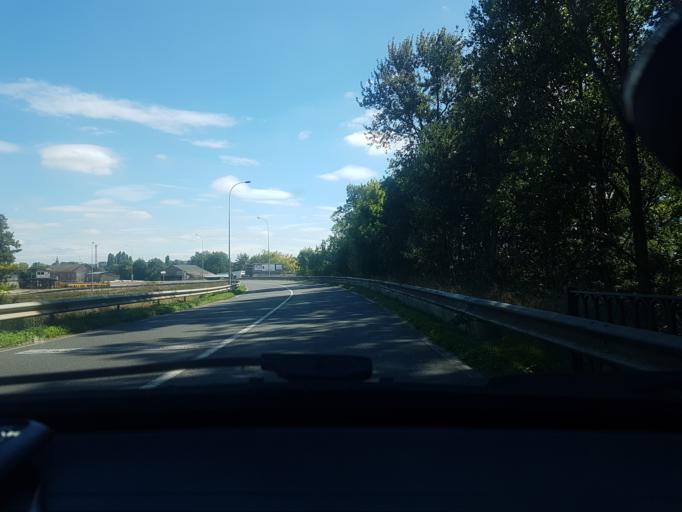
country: FR
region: Franche-Comte
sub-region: Departement de la Haute-Saone
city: Gray-la-Ville
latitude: 47.4488
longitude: 5.5644
